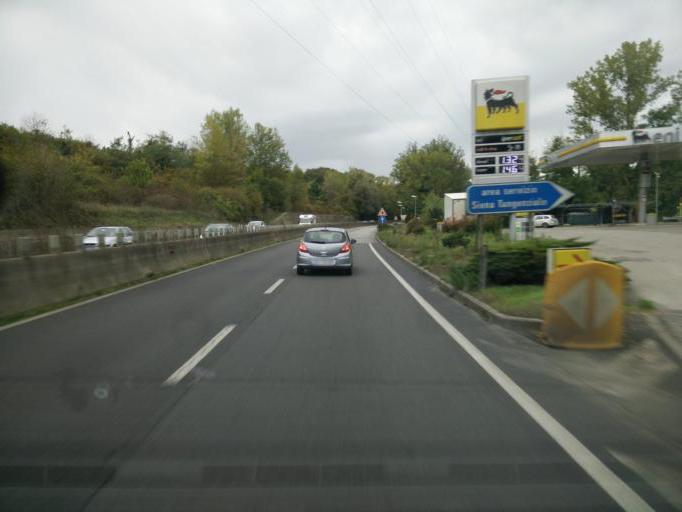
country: IT
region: Tuscany
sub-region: Provincia di Siena
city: Siena
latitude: 43.3156
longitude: 11.3054
